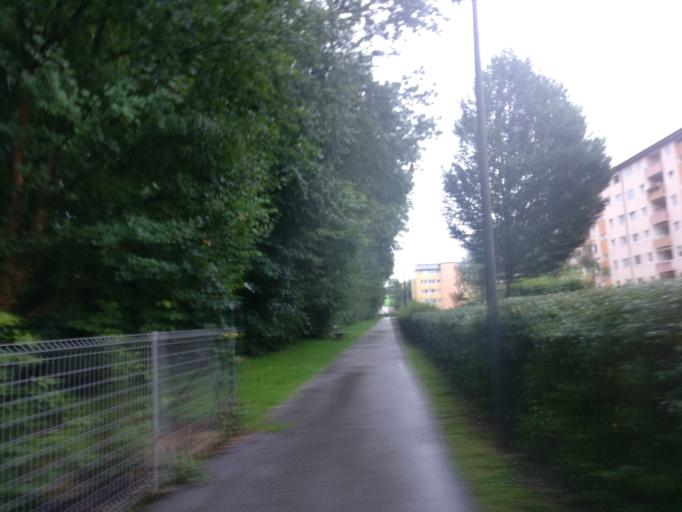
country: AT
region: Salzburg
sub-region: Politischer Bezirk Salzburg-Umgebung
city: Anif
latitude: 47.7821
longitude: 13.0717
